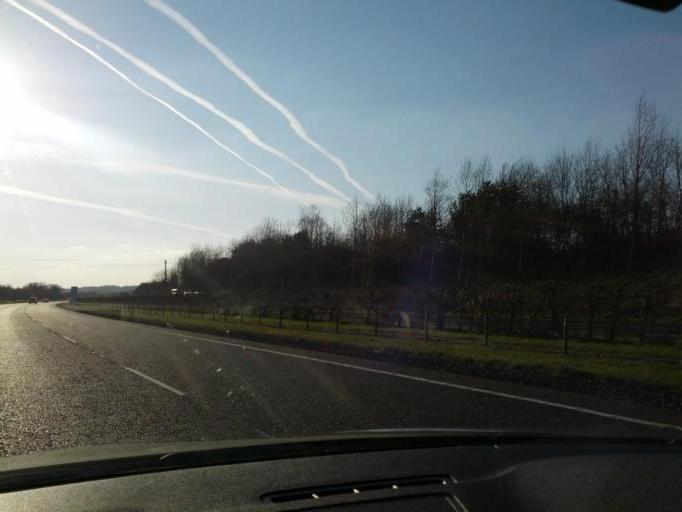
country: IE
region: Leinster
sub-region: Laois
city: Portlaoise
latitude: 53.0143
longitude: -7.2767
